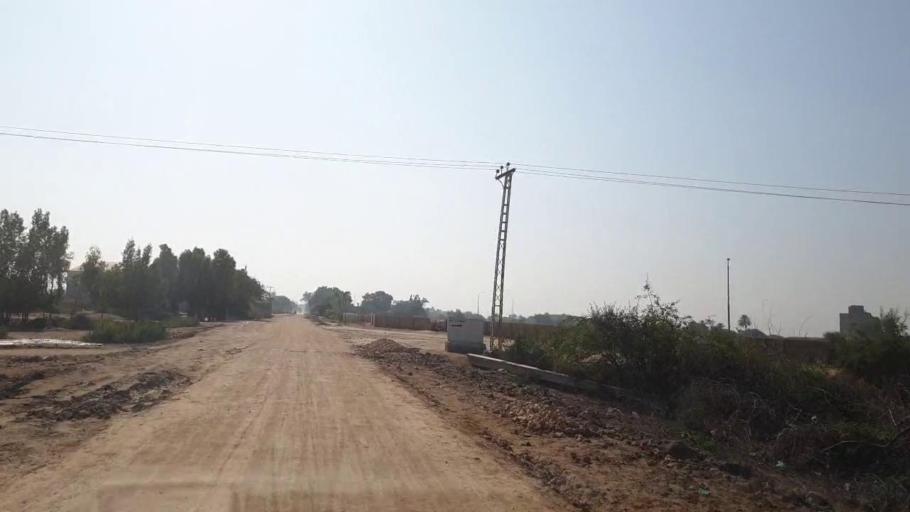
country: PK
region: Sindh
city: Thatta
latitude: 24.7600
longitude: 67.9162
